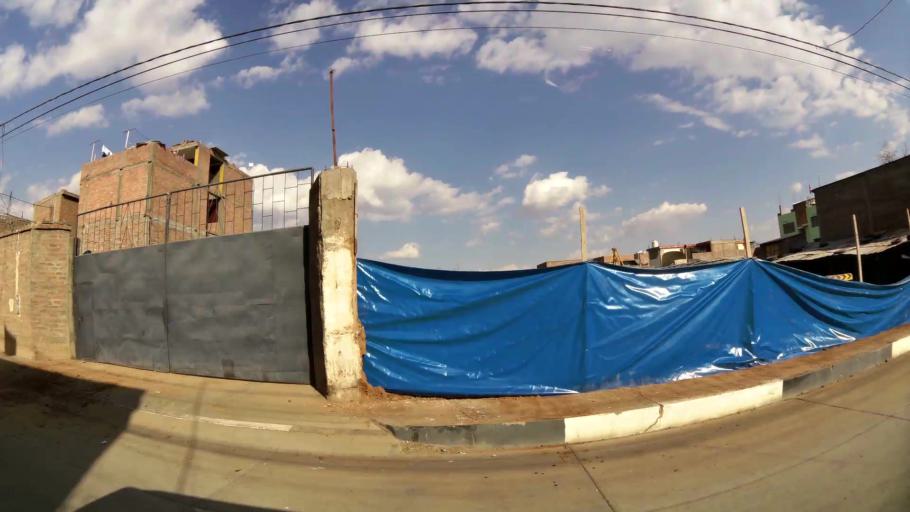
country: PE
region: Junin
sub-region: Provincia de Huancayo
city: El Tambo
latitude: -12.0578
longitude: -75.2281
